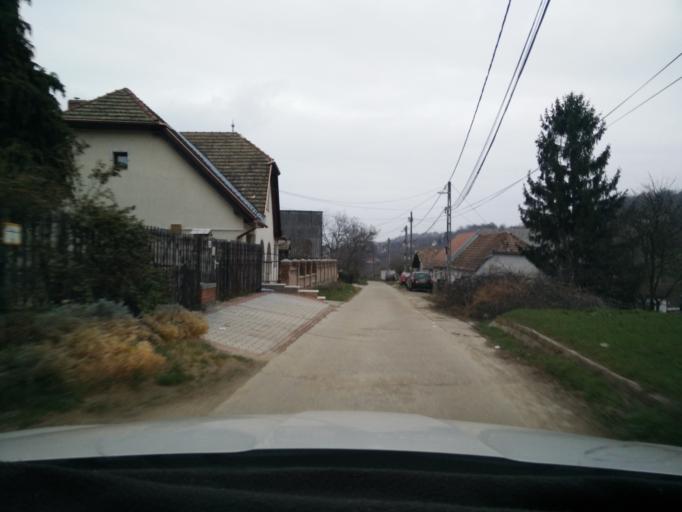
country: HU
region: Tolna
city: Szekszard
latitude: 46.3527
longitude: 18.6760
